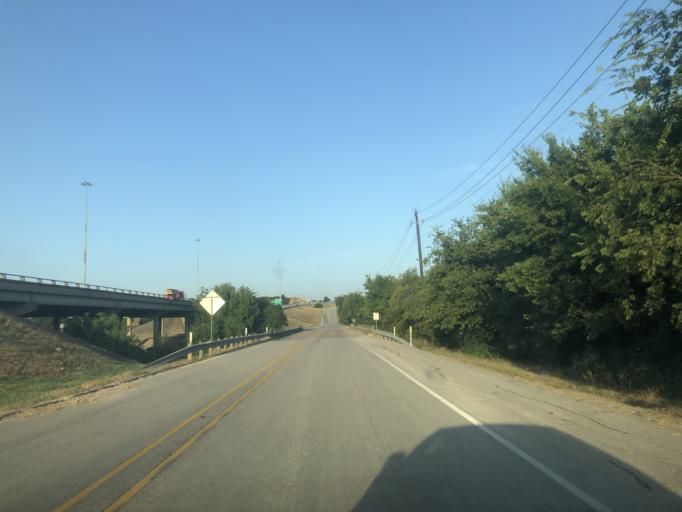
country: US
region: Texas
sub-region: Tarrant County
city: White Settlement
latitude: 32.7236
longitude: -97.5173
